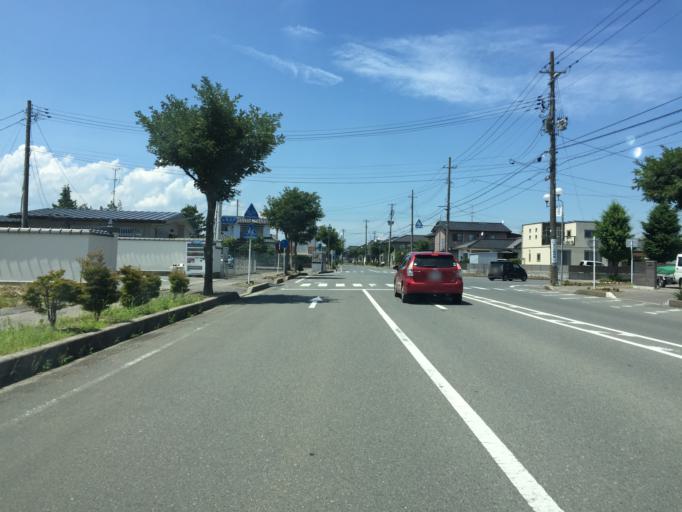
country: JP
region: Fukushima
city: Namie
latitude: 37.7046
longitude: 140.9634
